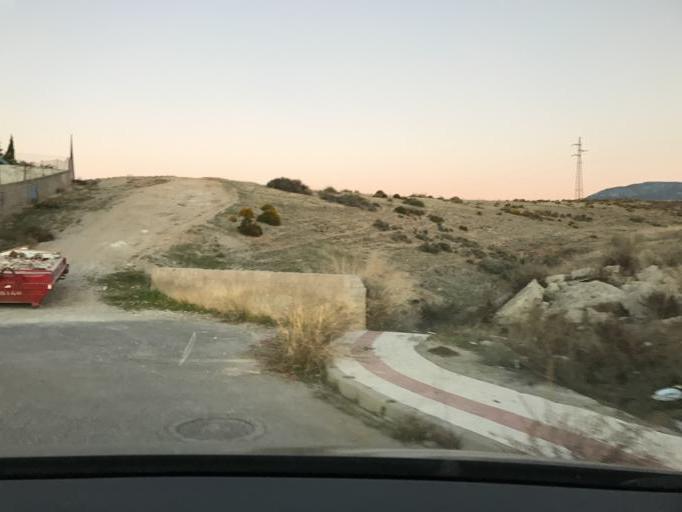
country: ES
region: Andalusia
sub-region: Provincia de Granada
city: Zubia
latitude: 37.1041
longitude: -3.5871
